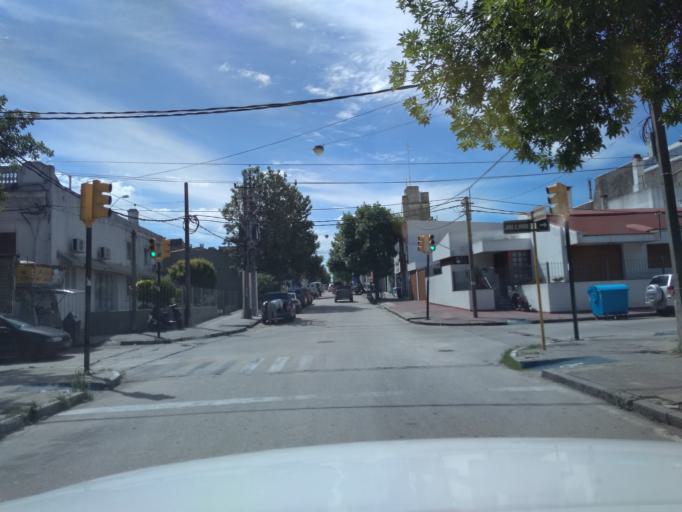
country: UY
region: Florida
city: Florida
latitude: -34.0978
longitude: -56.2147
